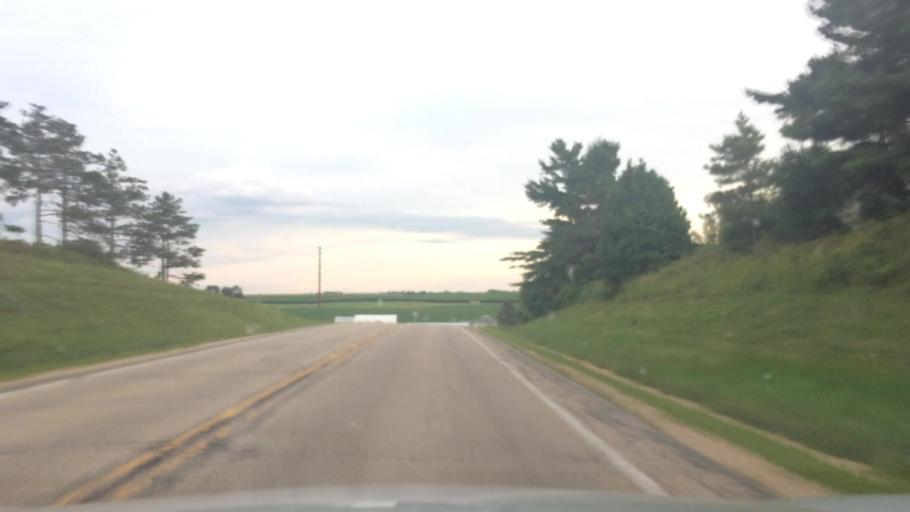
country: US
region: Wisconsin
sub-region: Columbia County
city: Lodi
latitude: 43.2333
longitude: -89.5410
